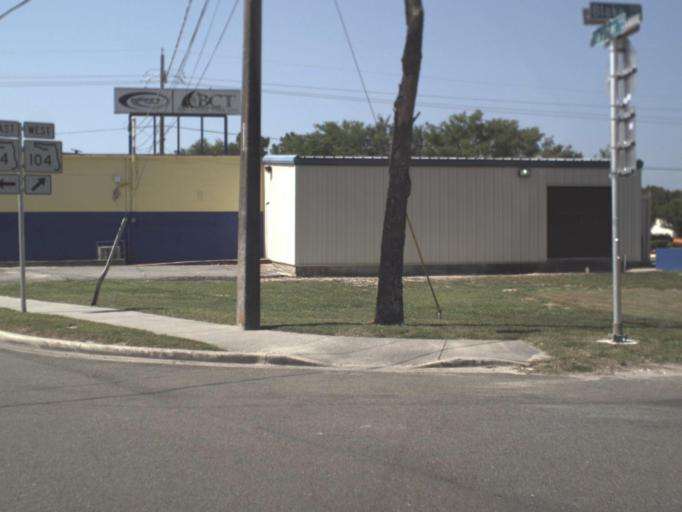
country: US
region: Florida
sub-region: Duval County
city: Jacksonville
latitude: 30.4395
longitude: -81.6986
